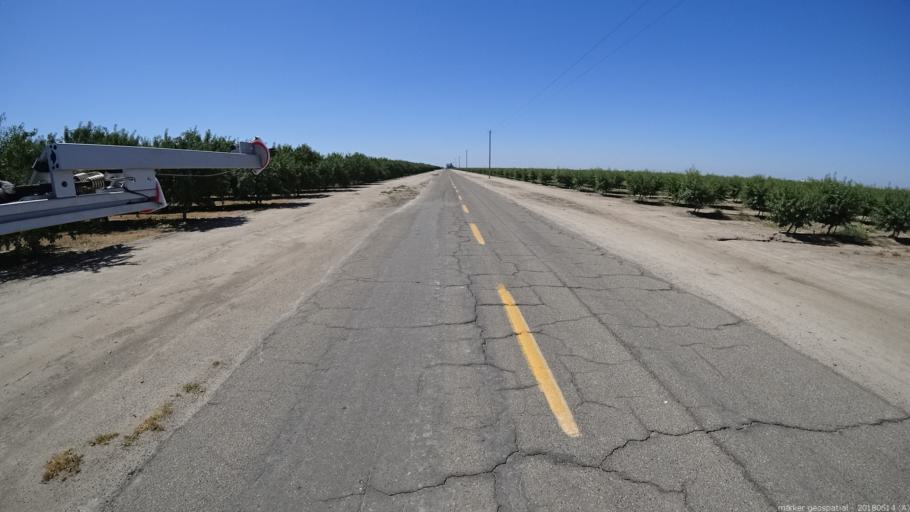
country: US
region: California
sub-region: Madera County
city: Fairmead
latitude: 36.9666
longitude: -120.1842
